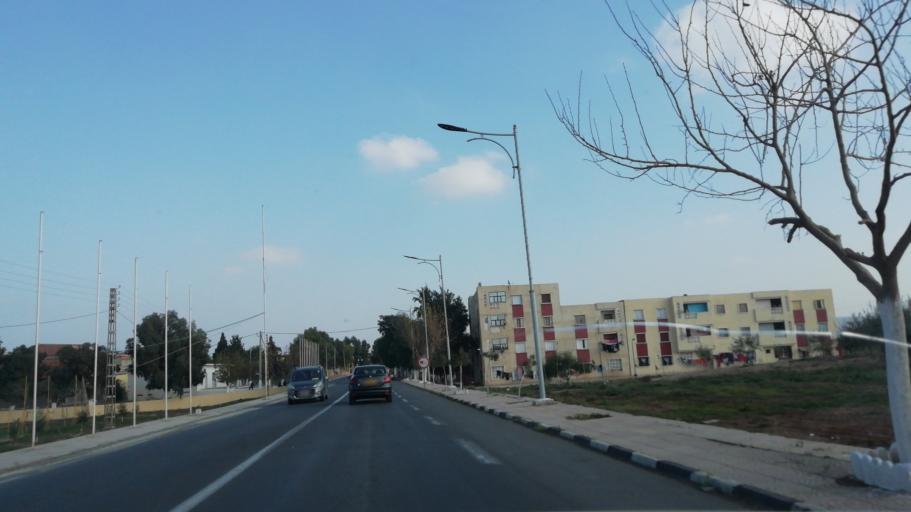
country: DZ
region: Ain Temouchent
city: Hammam Bou Hadjar
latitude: 35.3030
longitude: -1.0322
